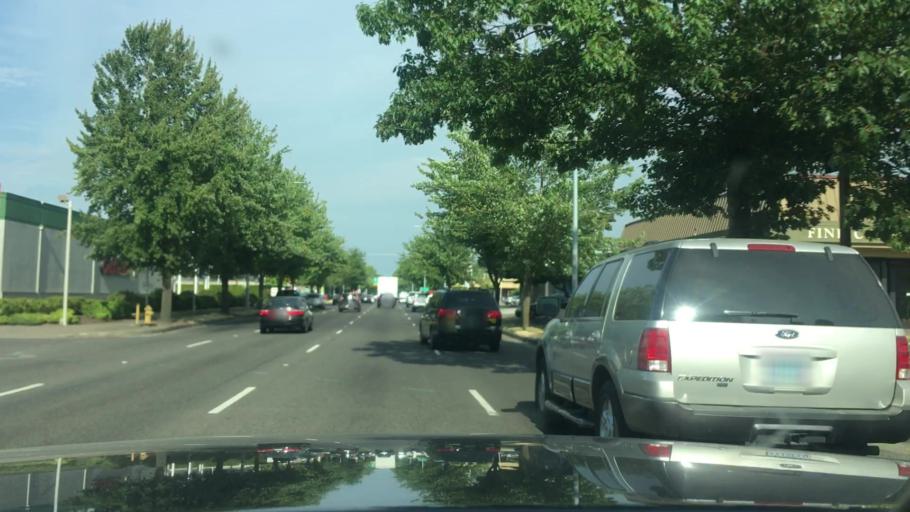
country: US
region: Oregon
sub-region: Lane County
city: Eugene
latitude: 44.0521
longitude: -123.1158
